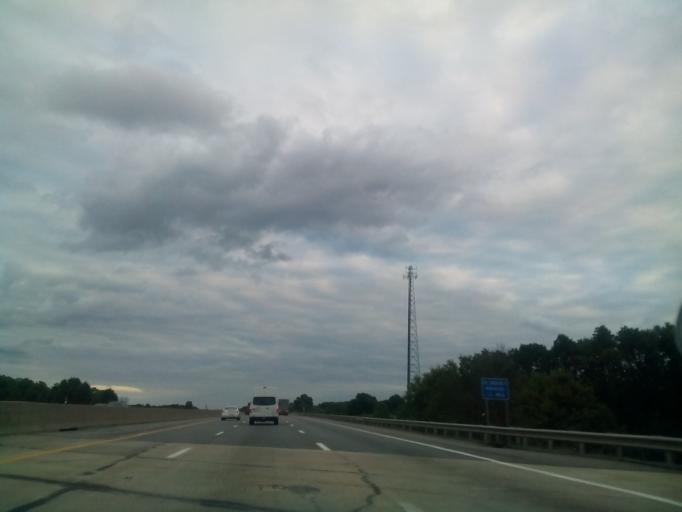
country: US
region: Ohio
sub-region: Trumbull County
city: Newton Falls
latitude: 41.1880
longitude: -80.9360
